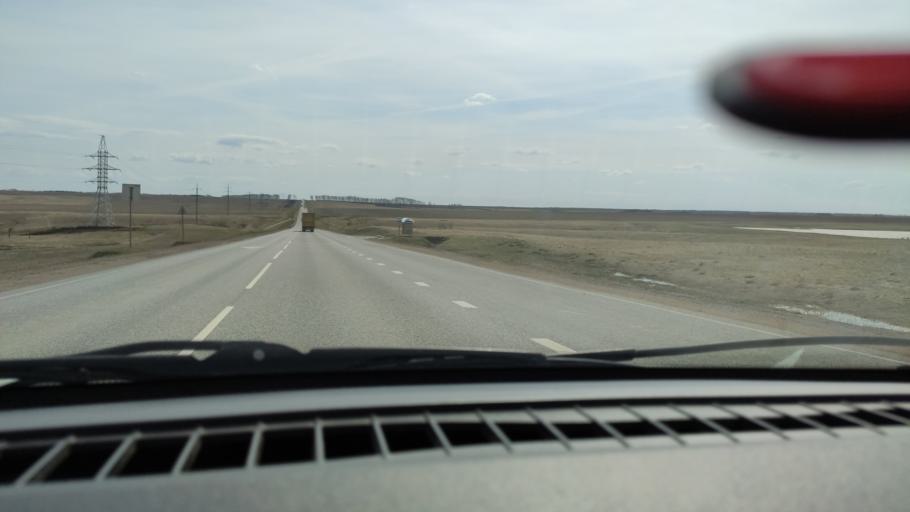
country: RU
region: Bashkortostan
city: Dyurtyuli
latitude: 55.3255
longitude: 54.9704
